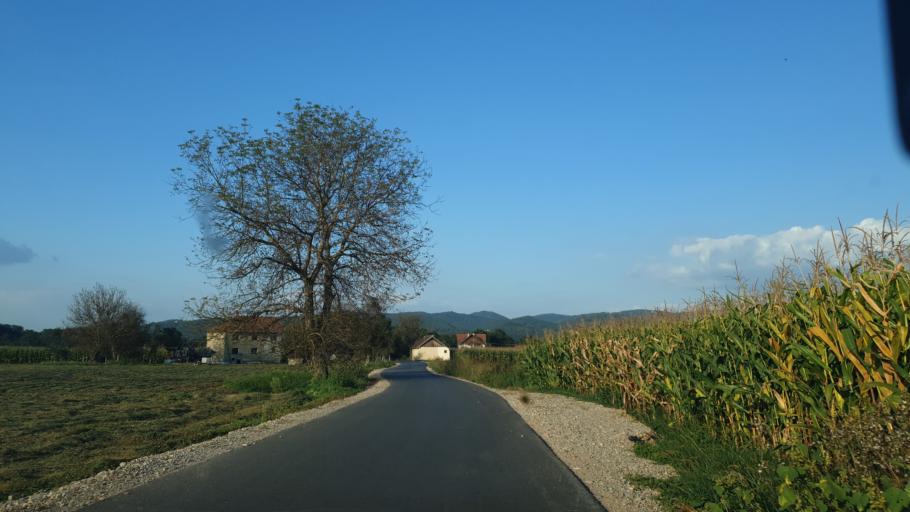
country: RS
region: Central Serbia
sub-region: Zlatiborski Okrug
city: Pozega
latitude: 43.8579
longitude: 19.9821
